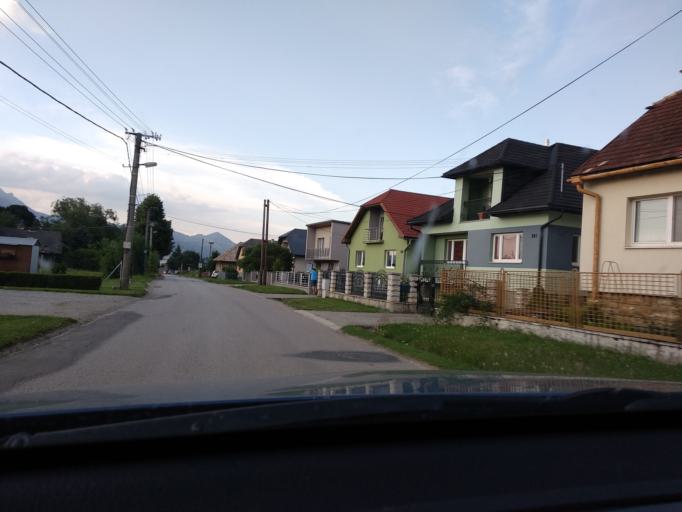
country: SK
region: Zilinsky
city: Ruzomberok
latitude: 49.0534
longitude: 19.3338
